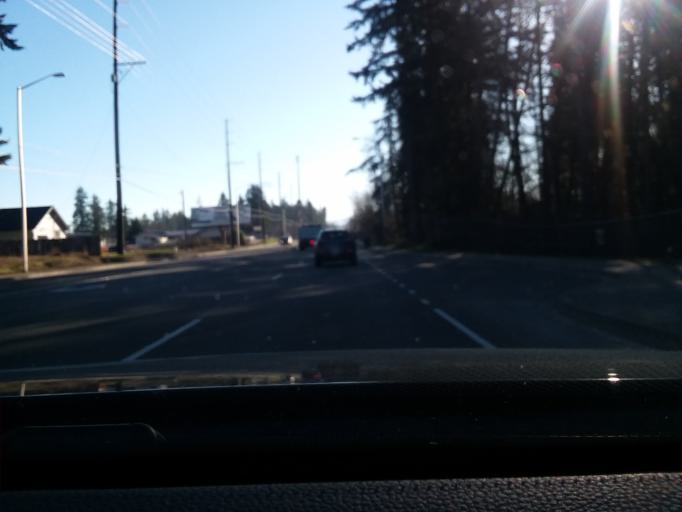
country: US
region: Washington
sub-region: Pierce County
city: Frederickson
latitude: 47.0964
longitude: -122.3421
